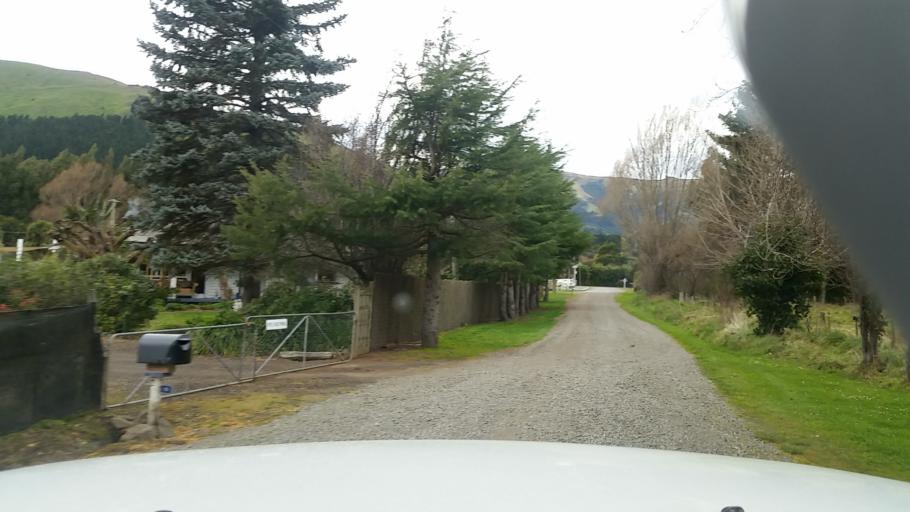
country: NZ
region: Canterbury
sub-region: Christchurch City
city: Christchurch
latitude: -43.7721
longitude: 172.7877
